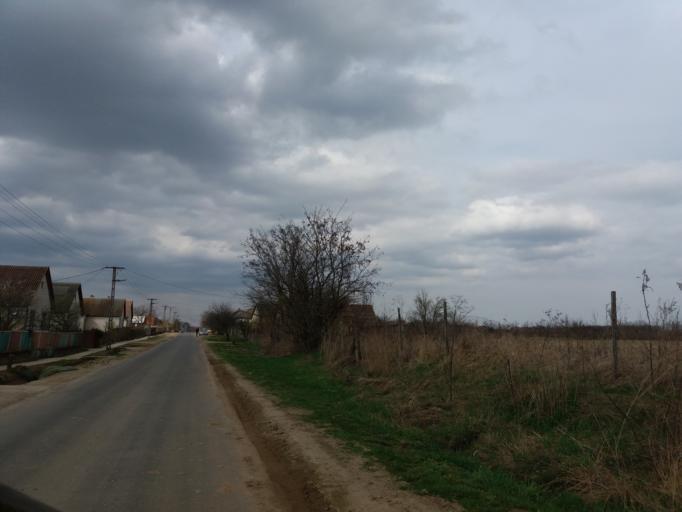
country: HU
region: Szabolcs-Szatmar-Bereg
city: Nyirtass
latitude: 48.0994
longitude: 22.0288
